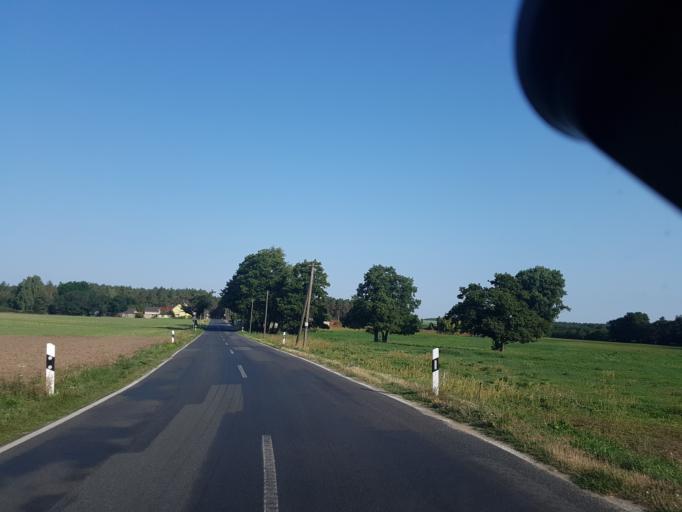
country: DE
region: Brandenburg
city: Niemegk
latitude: 52.1581
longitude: 12.6909
